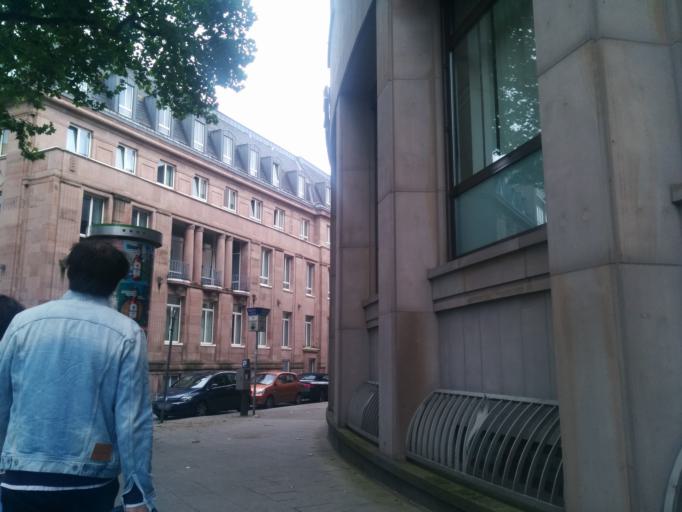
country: DE
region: North Rhine-Westphalia
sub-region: Regierungsbezirk Dusseldorf
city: Essen
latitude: 51.4530
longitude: 7.0110
